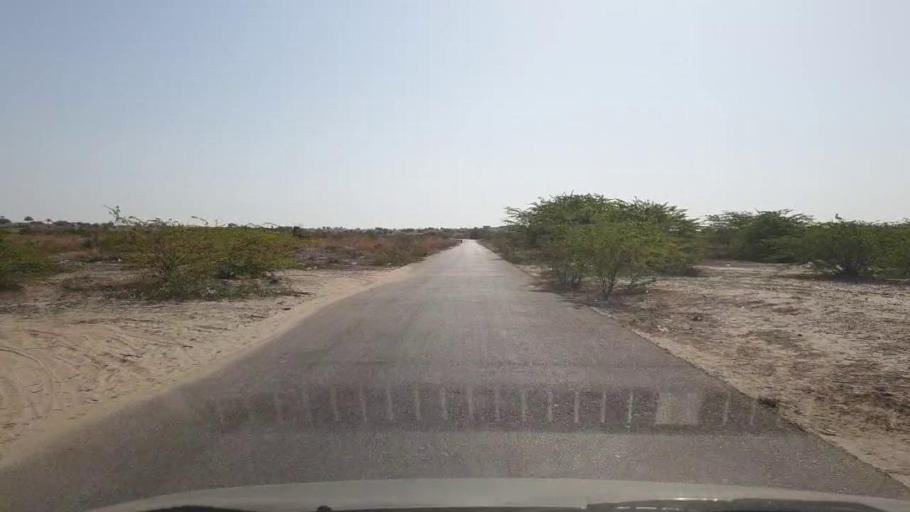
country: PK
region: Sindh
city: Chor
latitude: 25.4892
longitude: 69.7836
